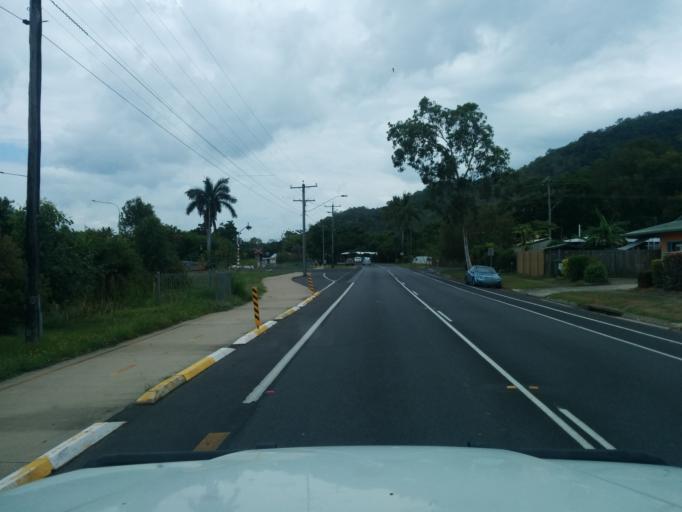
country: AU
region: Queensland
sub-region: Cairns
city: Cairns
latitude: -16.8831
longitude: 145.7458
